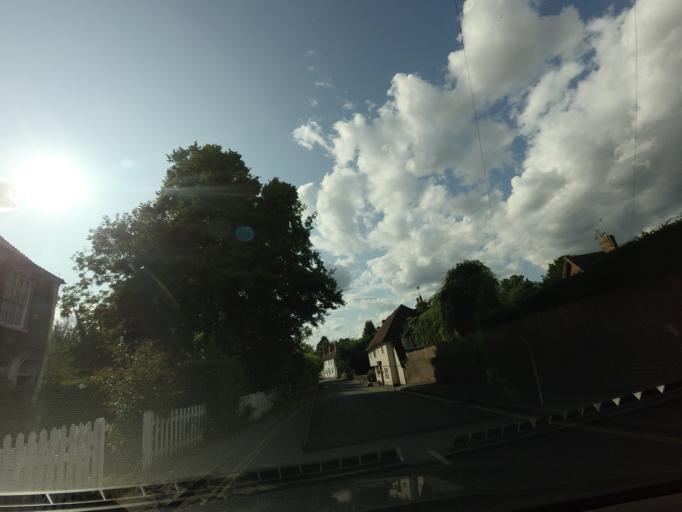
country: GB
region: England
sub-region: Kent
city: Harrietsham
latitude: 51.2613
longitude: 0.6286
